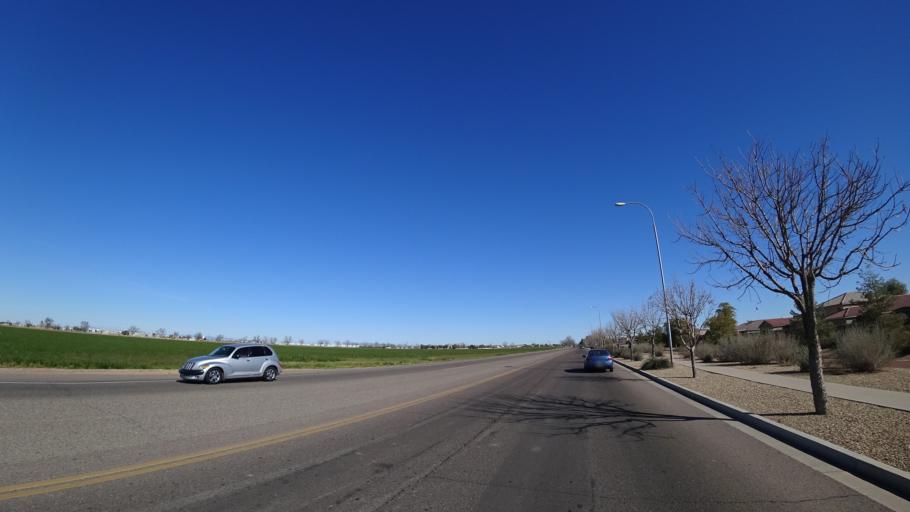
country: US
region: Arizona
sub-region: Maricopa County
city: Tolleson
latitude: 33.4211
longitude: -112.2678
